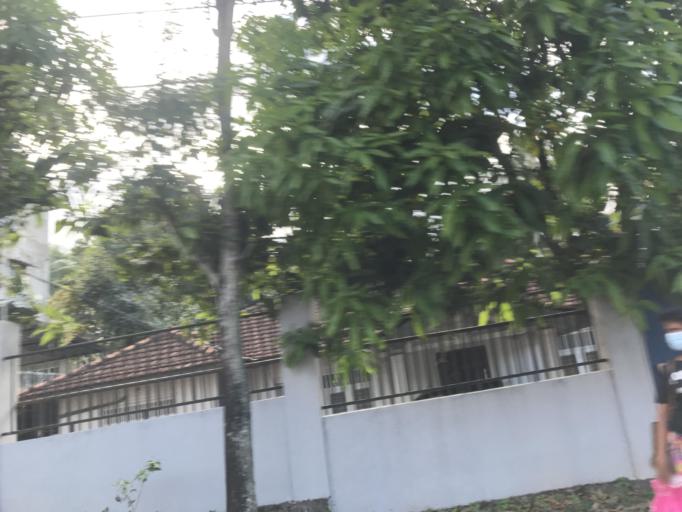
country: LK
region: Western
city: Gampaha
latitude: 7.0820
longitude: 79.9868
